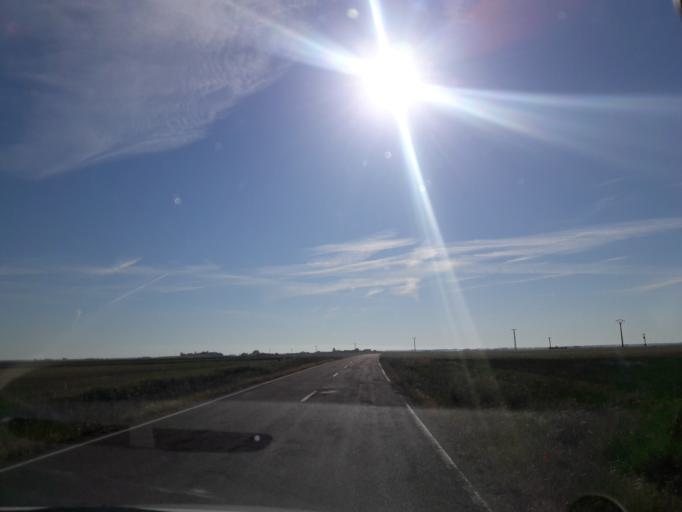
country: ES
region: Castille and Leon
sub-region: Provincia de Salamanca
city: Palencia de Negrilla
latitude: 41.0706
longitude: -5.6308
